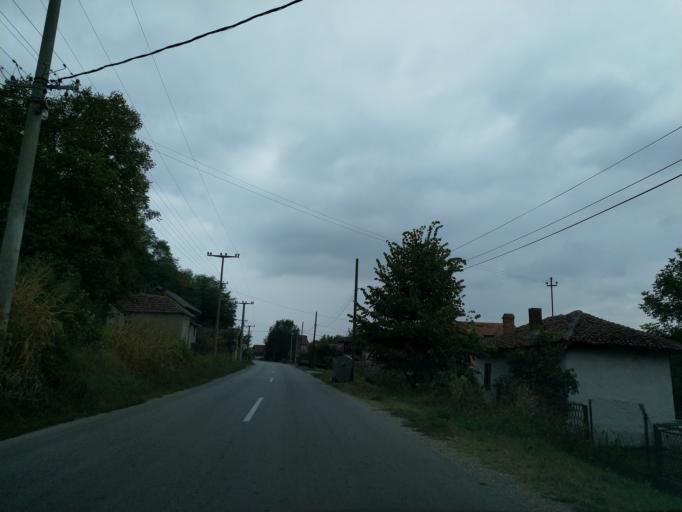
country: RS
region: Central Serbia
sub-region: Sumadijski Okrug
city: Batocina
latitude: 44.1033
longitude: 21.1623
